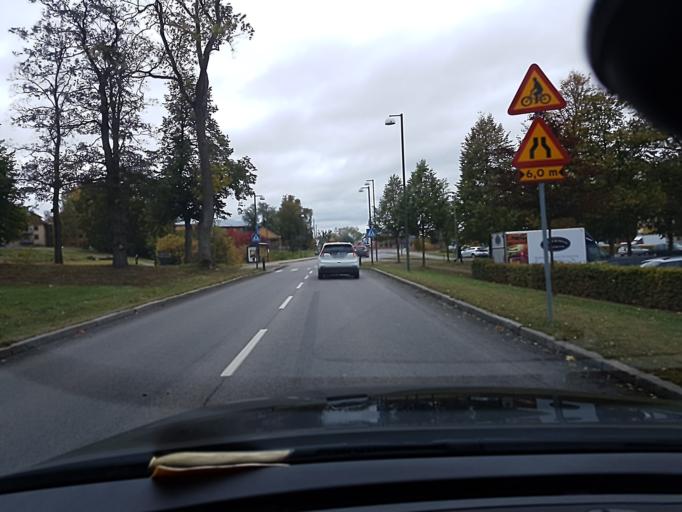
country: SE
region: Kronoberg
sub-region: Vaxjo Kommun
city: Vaexjoe
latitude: 56.8795
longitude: 14.8151
